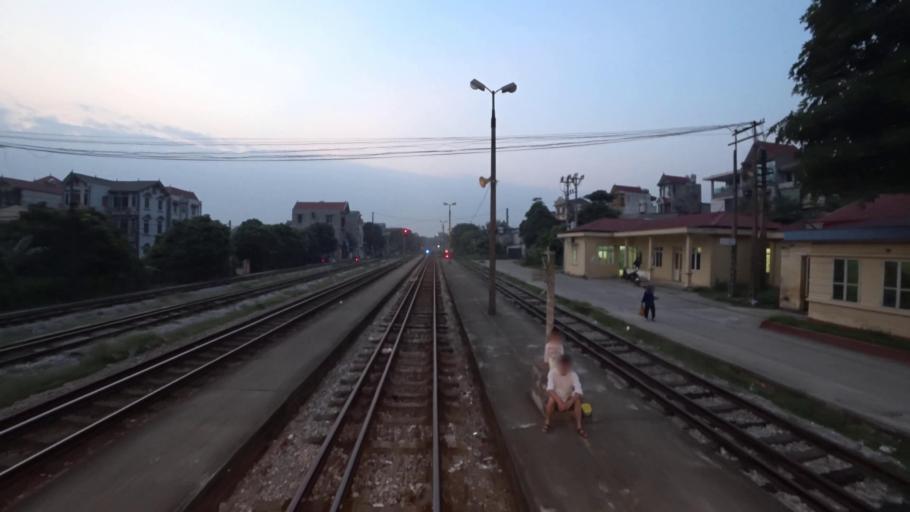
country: VN
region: Ha Noi
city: Soc Son
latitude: 21.2409
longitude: 105.8614
